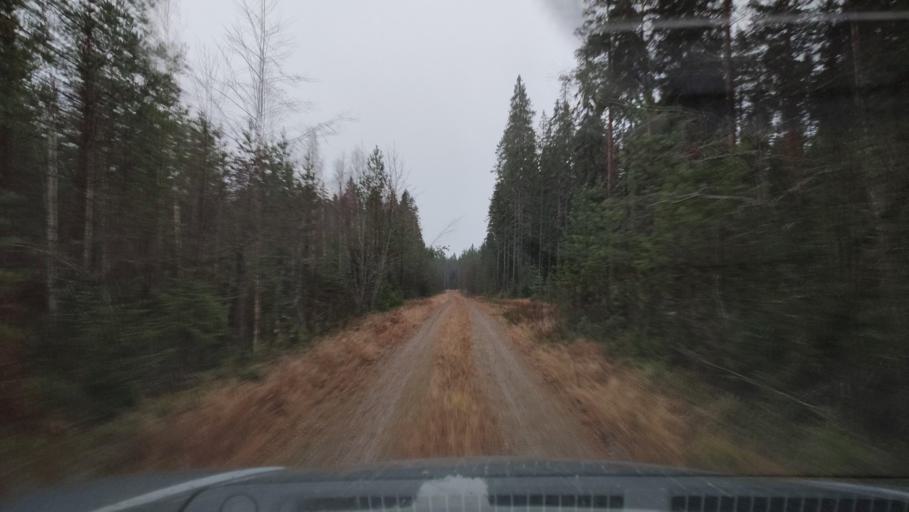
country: FI
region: Southern Ostrobothnia
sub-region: Suupohja
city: Karijoki
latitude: 62.1483
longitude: 21.5917
